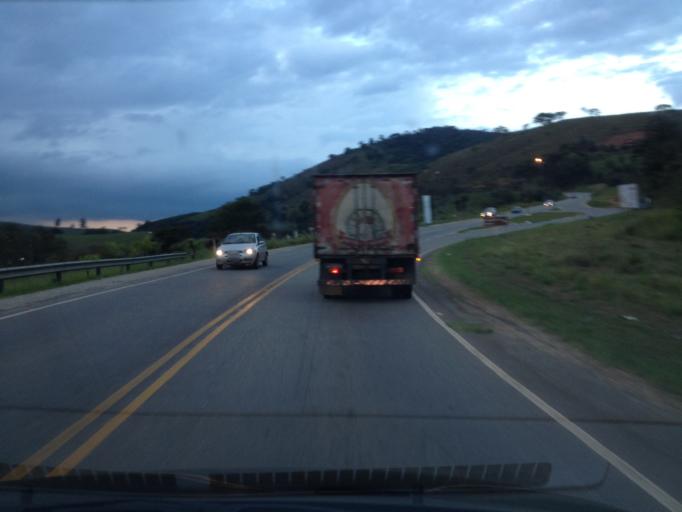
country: BR
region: Minas Gerais
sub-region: Sao Lourenco
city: Sao Lourenco
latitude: -22.0581
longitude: -45.0385
